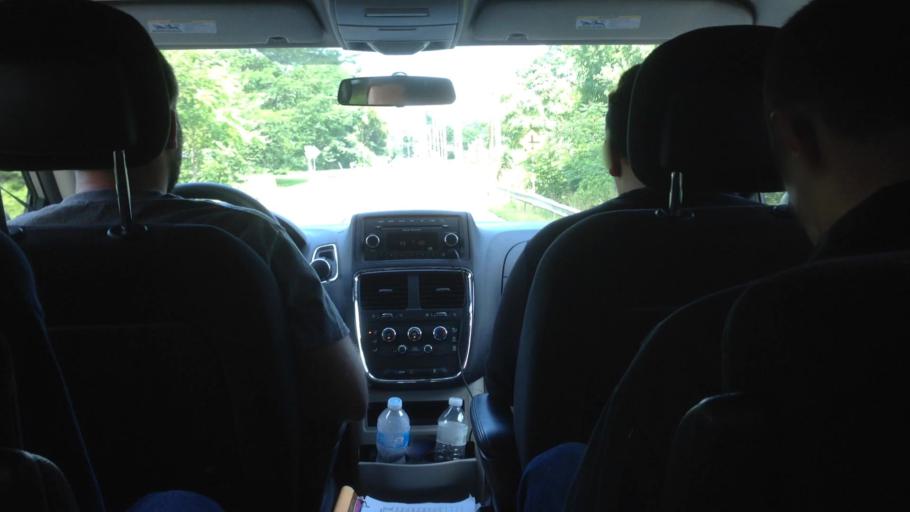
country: US
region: New York
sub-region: Dutchess County
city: Red Hook
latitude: 42.0267
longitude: -73.8477
